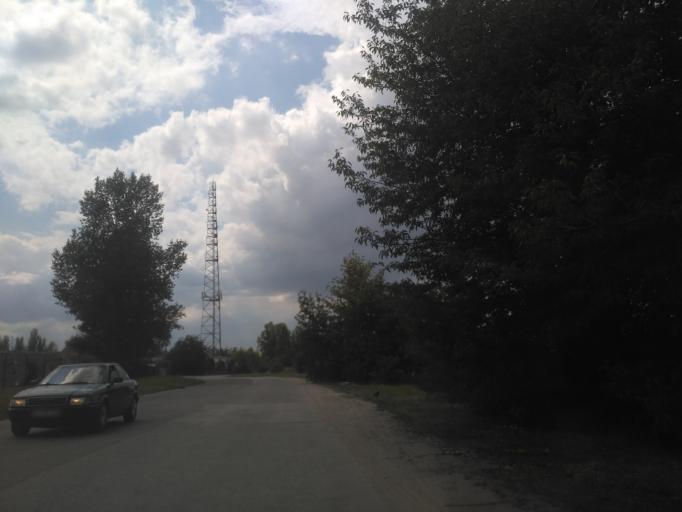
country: PL
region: Lublin Voivodeship
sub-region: Powiat lubelski
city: Jakubowice Murowane
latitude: 51.2363
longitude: 22.6183
